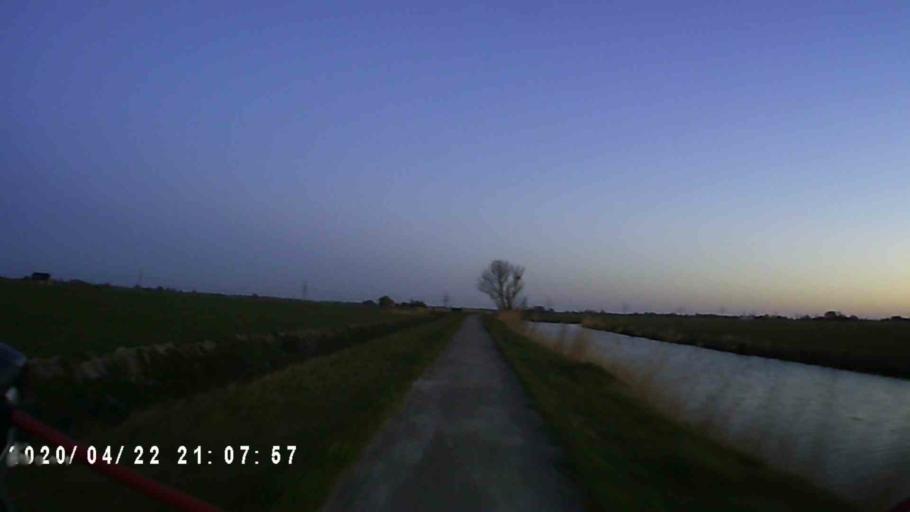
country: NL
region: Groningen
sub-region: Gemeente Winsum
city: Winsum
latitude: 53.3157
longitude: 6.5610
